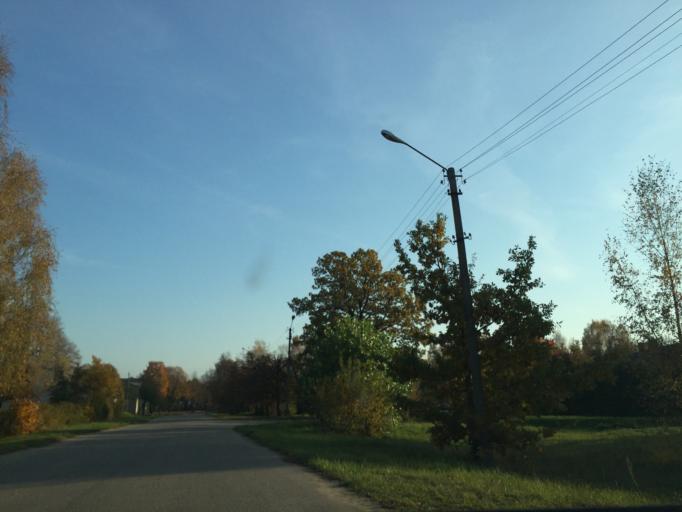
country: LV
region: Skrunda
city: Skrunda
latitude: 56.6784
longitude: 22.0128
